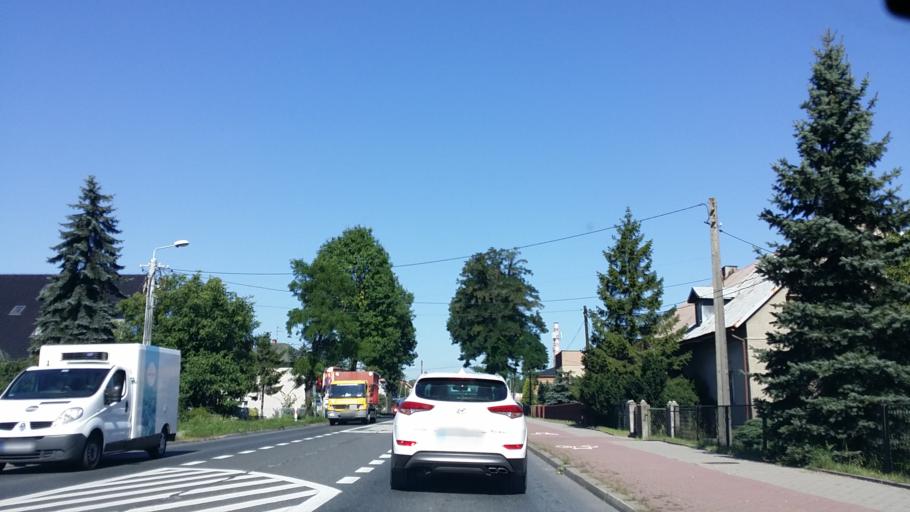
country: PL
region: Lesser Poland Voivodeship
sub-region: Powiat oswiecimski
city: Babice
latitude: 50.0690
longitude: 19.1865
